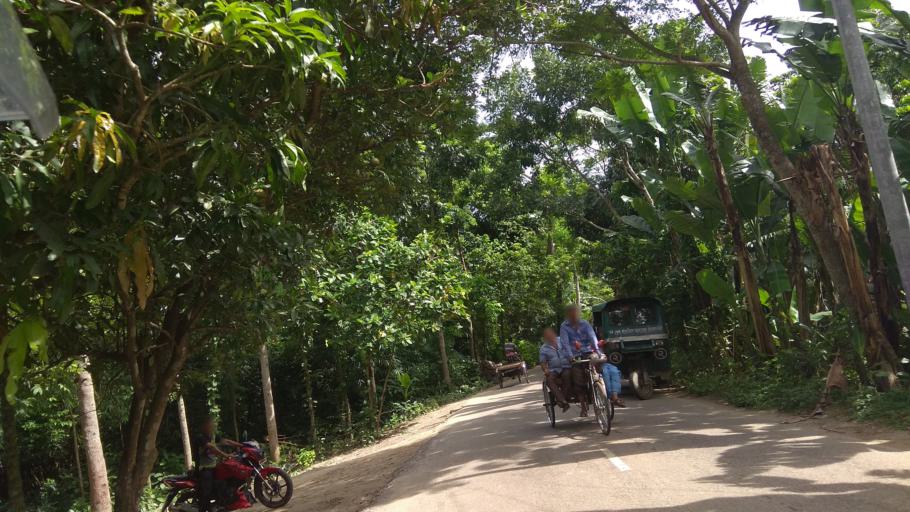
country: BD
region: Khulna
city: Kalia
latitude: 23.1533
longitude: 89.6445
